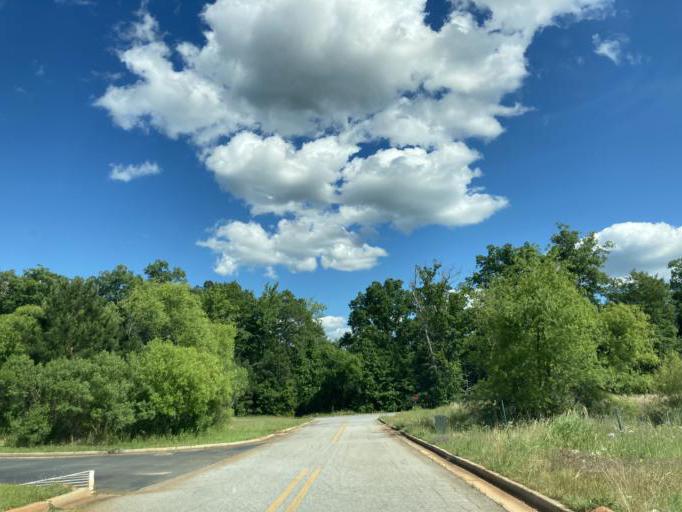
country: US
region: Georgia
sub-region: Jones County
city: Gray
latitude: 33.0015
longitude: -83.5483
